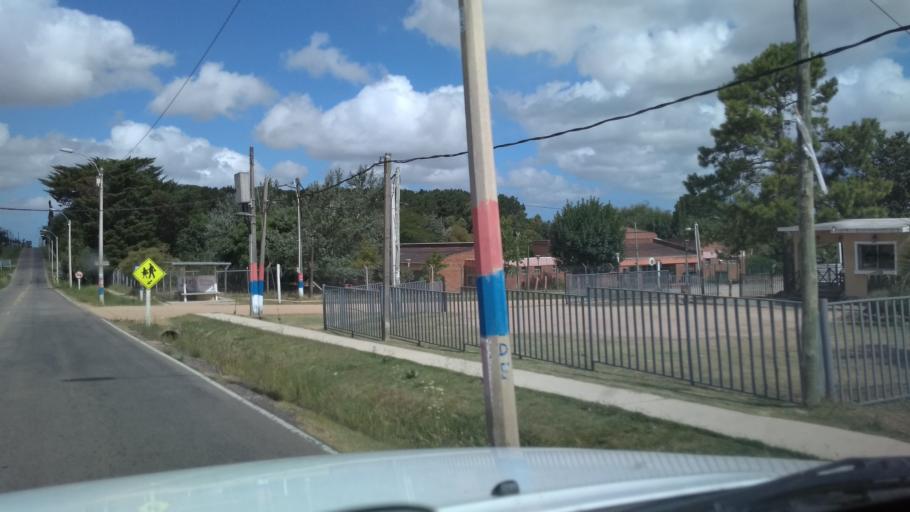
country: UY
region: Canelones
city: Joaquin Suarez
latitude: -34.7157
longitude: -56.0513
